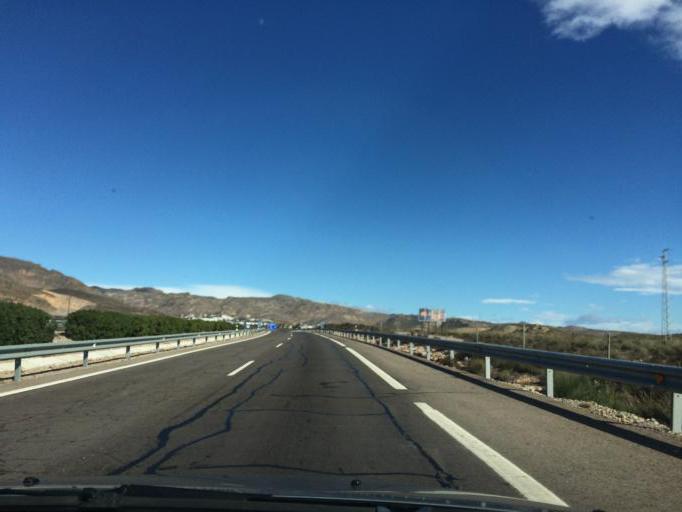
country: ES
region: Andalusia
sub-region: Provincia de Almeria
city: Nijar
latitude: 36.9258
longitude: -2.2098
